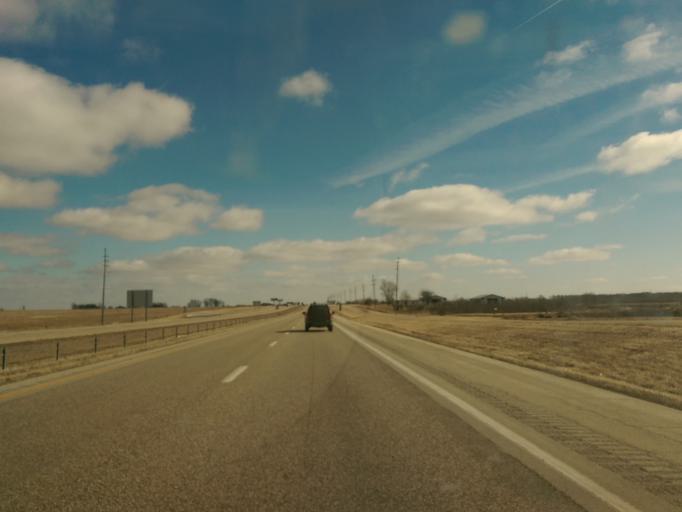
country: US
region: Missouri
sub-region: Montgomery County
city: Montgomery City
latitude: 38.8917
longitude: -91.4289
